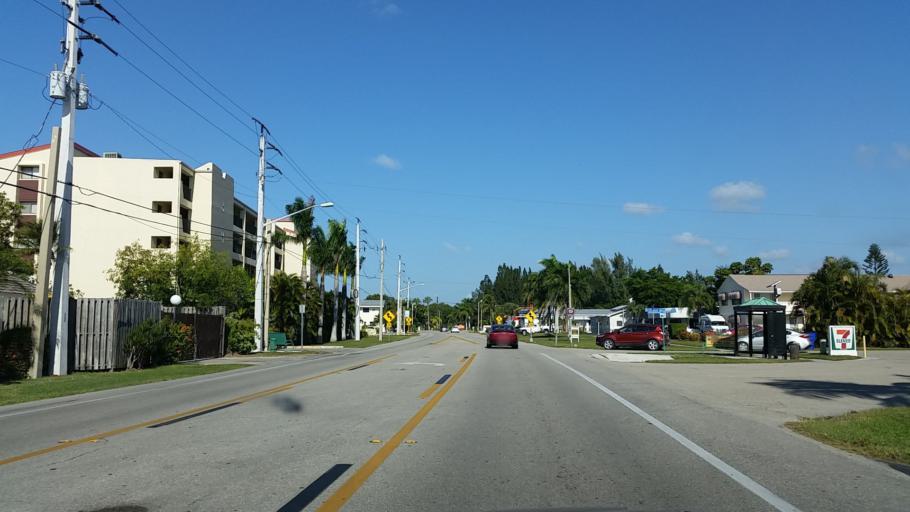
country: US
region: Florida
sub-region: Lee County
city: Fort Myers Beach
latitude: 26.4236
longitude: -81.9051
